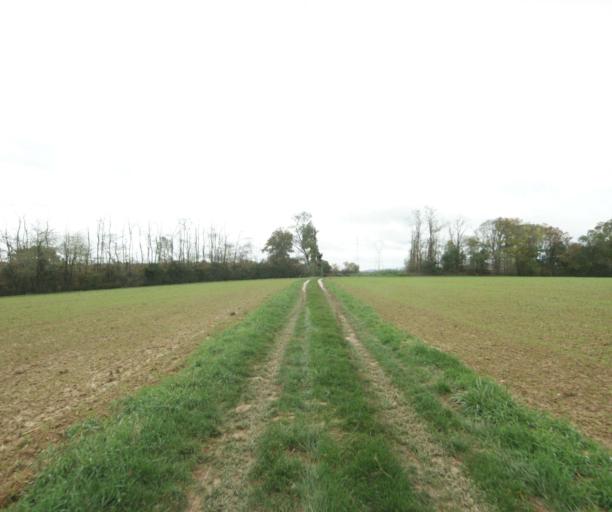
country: FR
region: Bourgogne
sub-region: Departement de Saone-et-Loire
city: Saint-Martin-Belle-Roche
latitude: 46.4598
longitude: 4.8660
